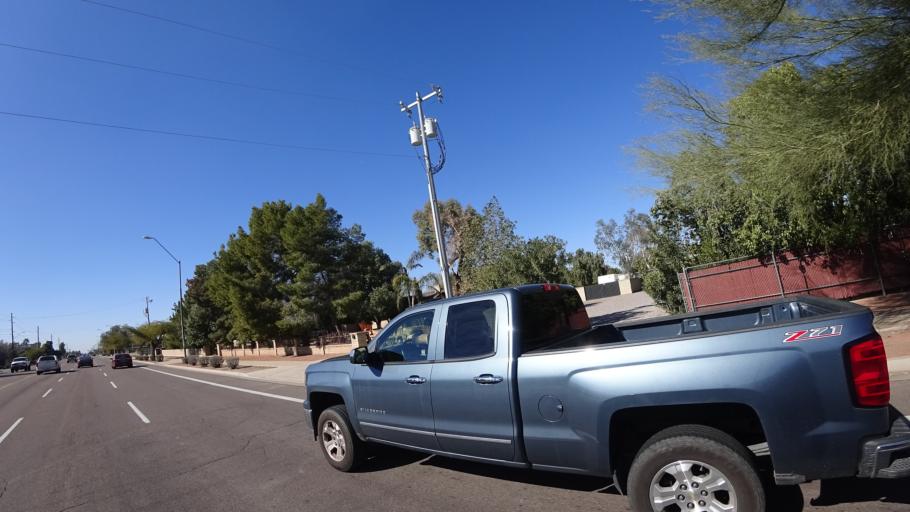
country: US
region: Arizona
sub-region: Maricopa County
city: Peoria
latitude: 33.6546
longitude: -112.1461
